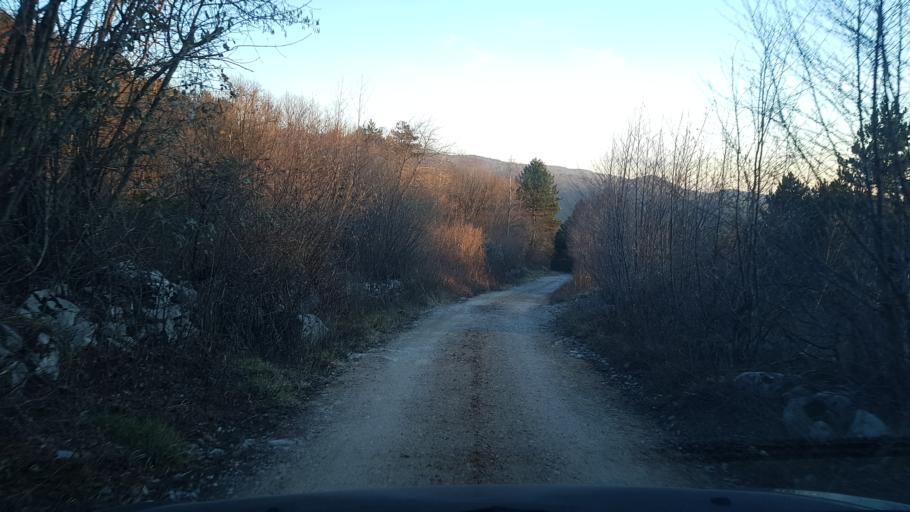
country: SI
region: Nova Gorica
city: Kromberk
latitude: 46.0159
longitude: 13.7019
